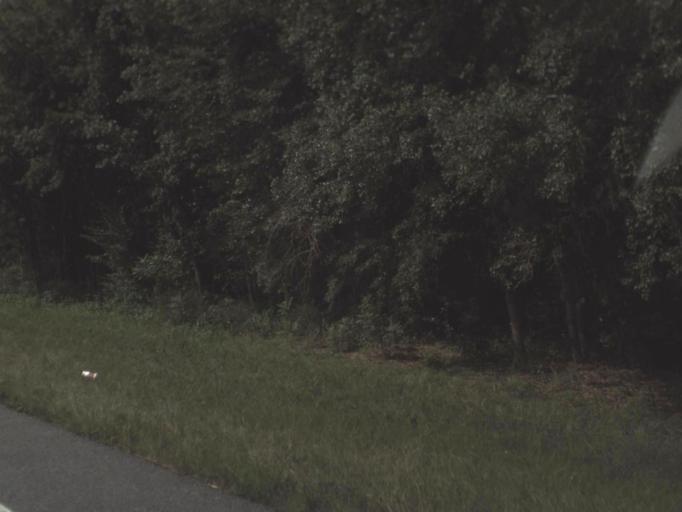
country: US
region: Florida
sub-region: Citrus County
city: Citrus Springs
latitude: 29.0007
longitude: -82.4452
